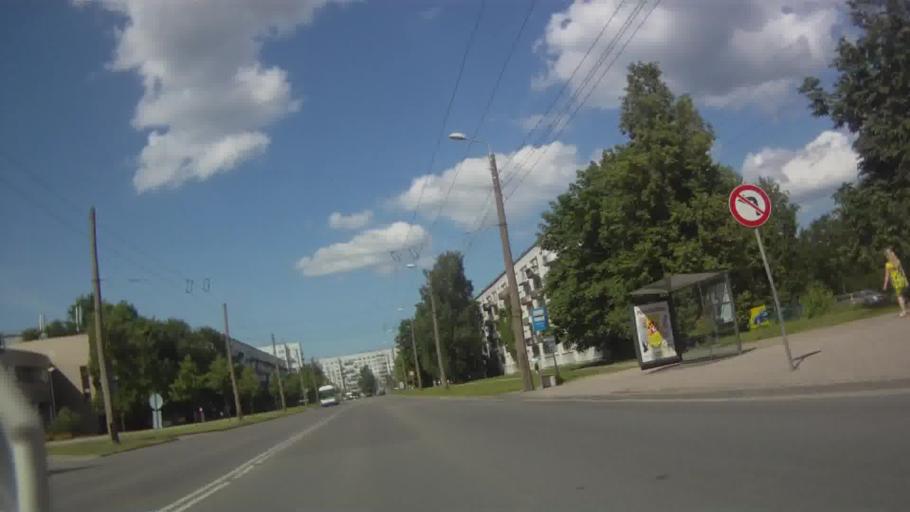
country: LV
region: Riga
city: Riga
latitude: 56.9554
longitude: 24.1757
